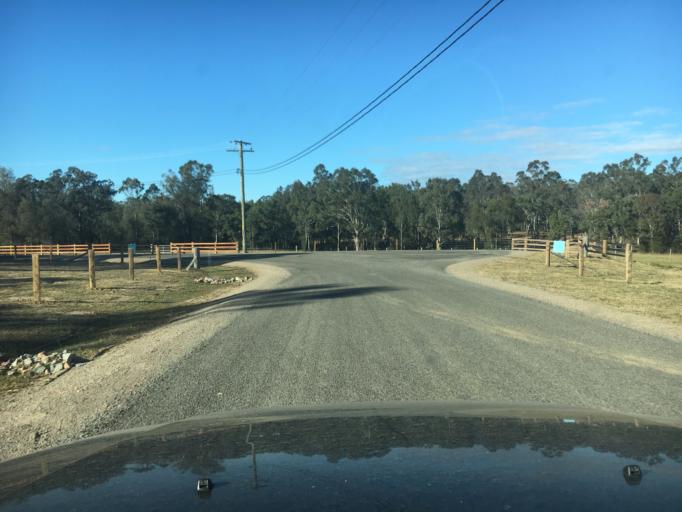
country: AU
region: New South Wales
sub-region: Singleton
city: Singleton
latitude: -32.5349
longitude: 151.2253
